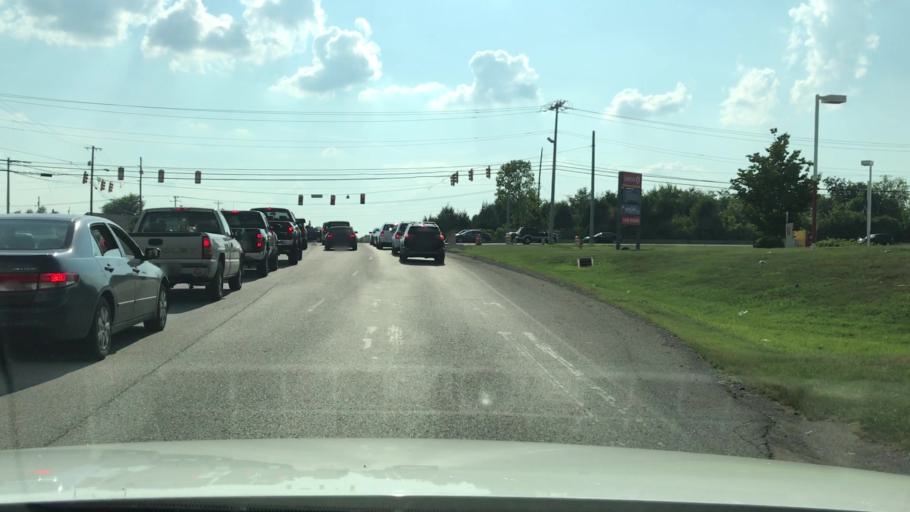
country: US
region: Tennessee
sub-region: Sumner County
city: Gallatin
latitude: 36.3637
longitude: -86.4390
